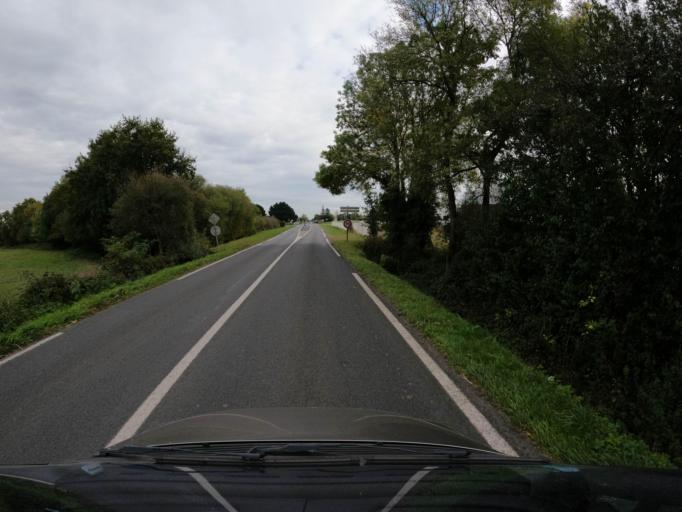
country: FR
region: Pays de la Loire
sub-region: Departement de la Loire-Atlantique
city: Boussay
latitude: 47.0609
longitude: -1.1880
